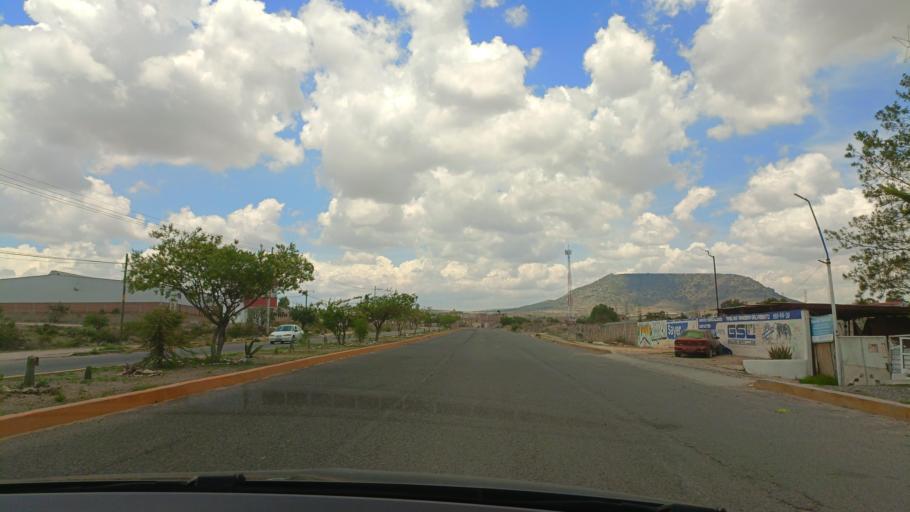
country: MX
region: Guanajuato
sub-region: San Luis de la Paz
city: San Luis de la Paz
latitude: 21.2933
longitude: -100.4901
